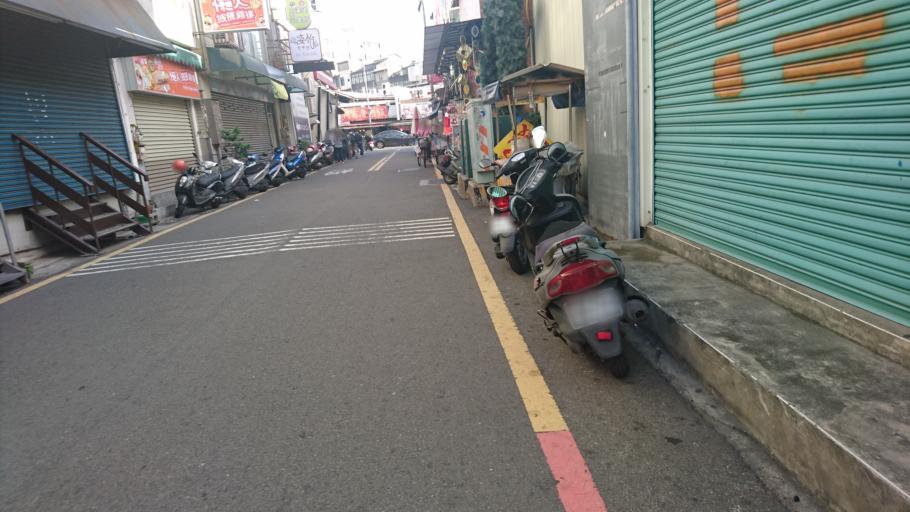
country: TW
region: Taiwan
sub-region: Hsinchu
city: Hsinchu
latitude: 24.8050
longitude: 120.9652
